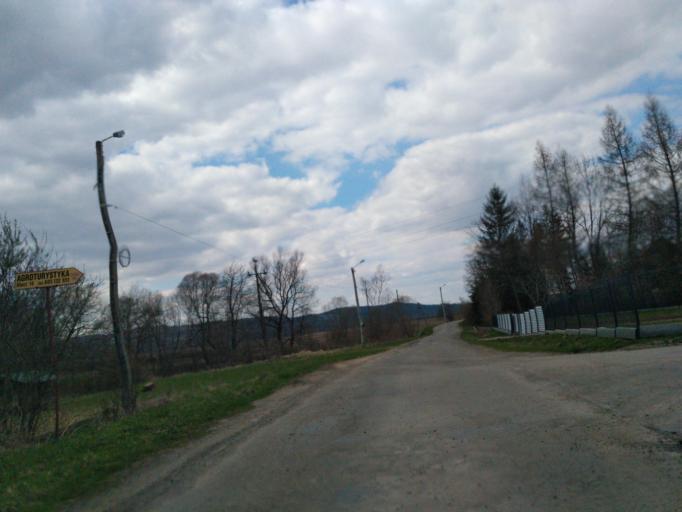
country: PL
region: Subcarpathian Voivodeship
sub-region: Powiat sanocki
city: Tyrawa Woloska
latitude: 49.6647
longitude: 22.2916
